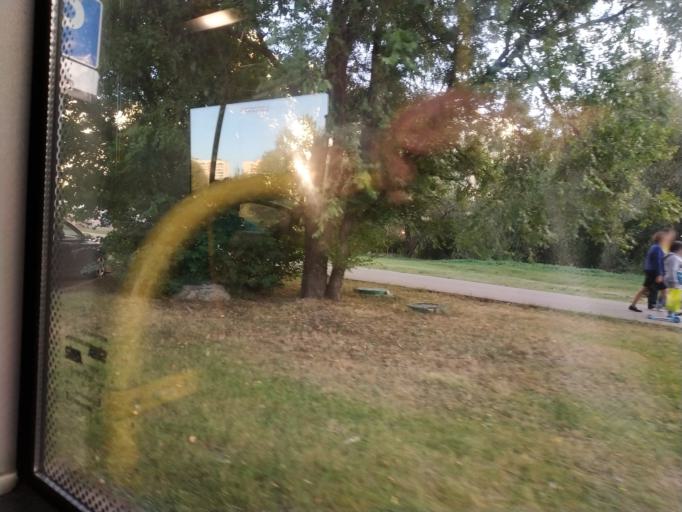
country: RU
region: Moscow
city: Novo-Peredelkino
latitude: 55.6434
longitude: 37.3549
